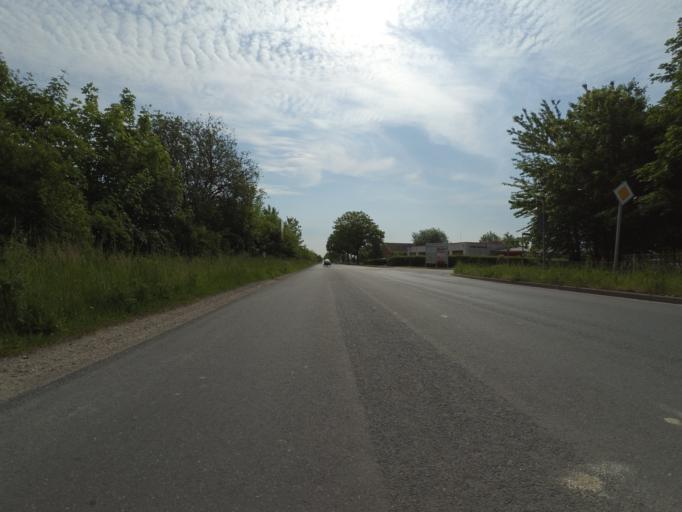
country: DE
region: Lower Saxony
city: Lehrte
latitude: 52.3681
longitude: 9.9928
